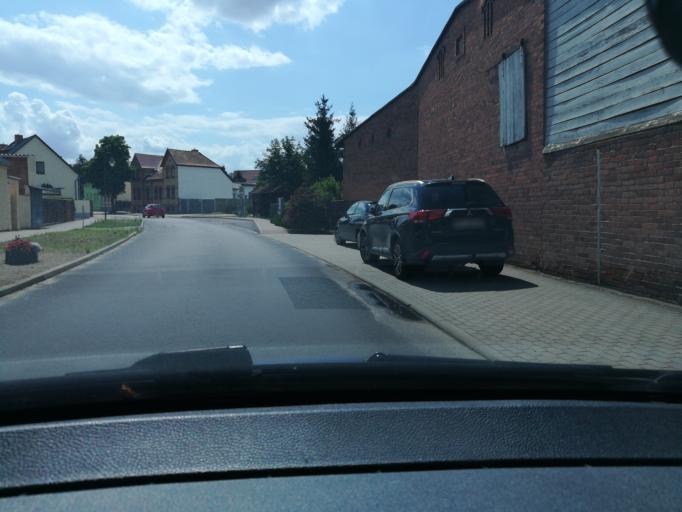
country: DE
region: Saxony-Anhalt
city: Rogatz
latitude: 52.3170
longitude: 11.7660
